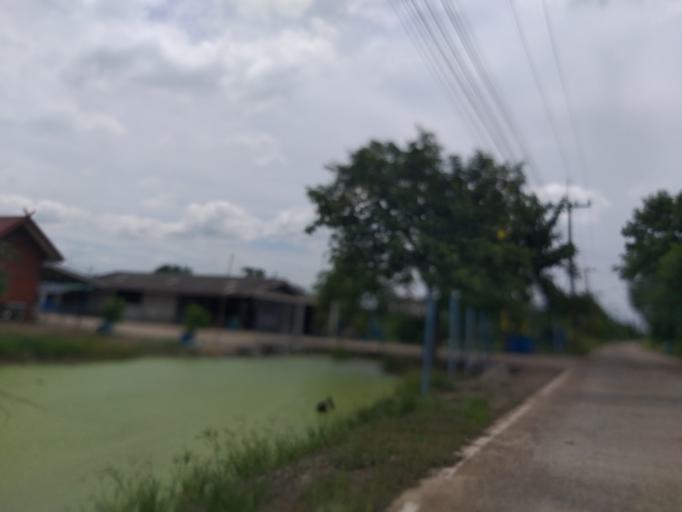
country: TH
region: Pathum Thani
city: Ban Lam Luk Ka
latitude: 13.9793
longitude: 100.8541
